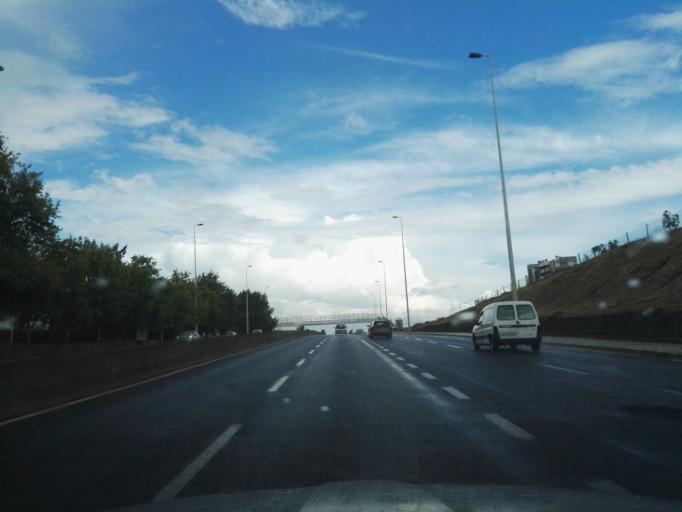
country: PT
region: Lisbon
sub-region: Loures
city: Moscavide
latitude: 38.7623
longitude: -9.1249
